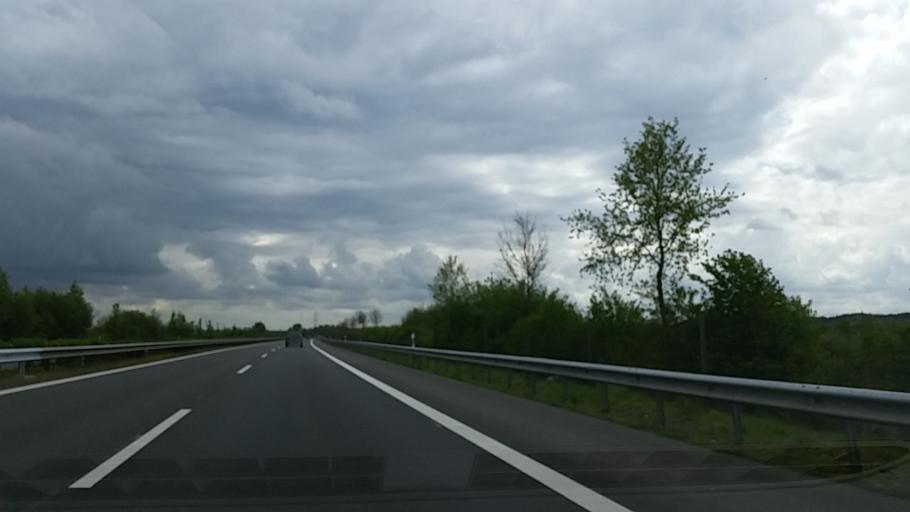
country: DE
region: Lower Saxony
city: Horneburg
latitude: 53.5331
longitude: 9.5785
